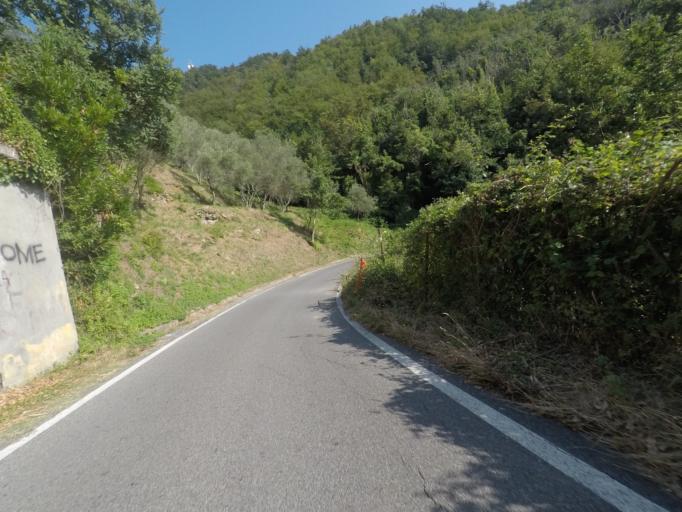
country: IT
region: Liguria
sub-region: Provincia di La Spezia
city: Casano-Dogana-Isola
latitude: 44.0854
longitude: 10.0550
